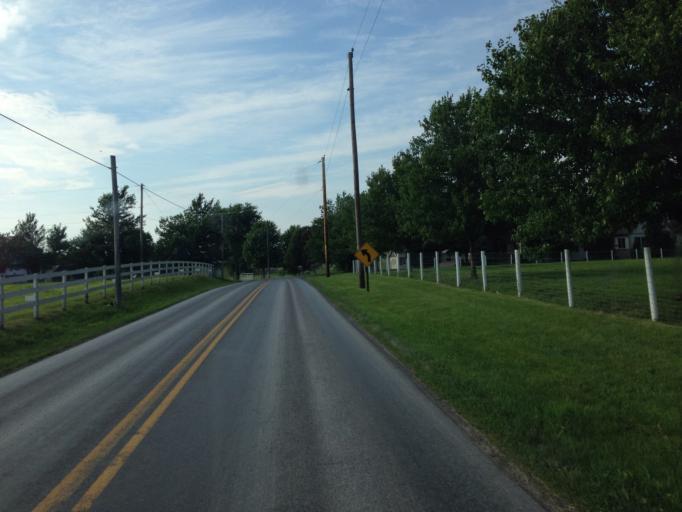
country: US
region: Pennsylvania
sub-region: Lancaster County
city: Strasburg
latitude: 40.0514
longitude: -76.1890
